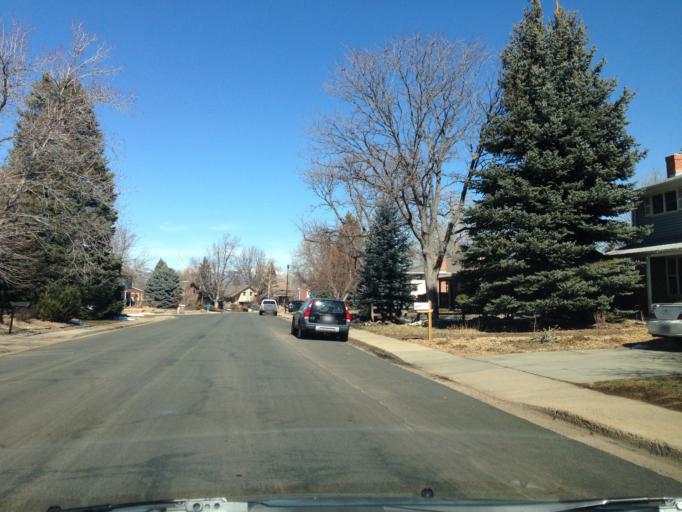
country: US
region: Colorado
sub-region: Boulder County
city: Boulder
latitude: 39.9901
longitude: -105.2282
